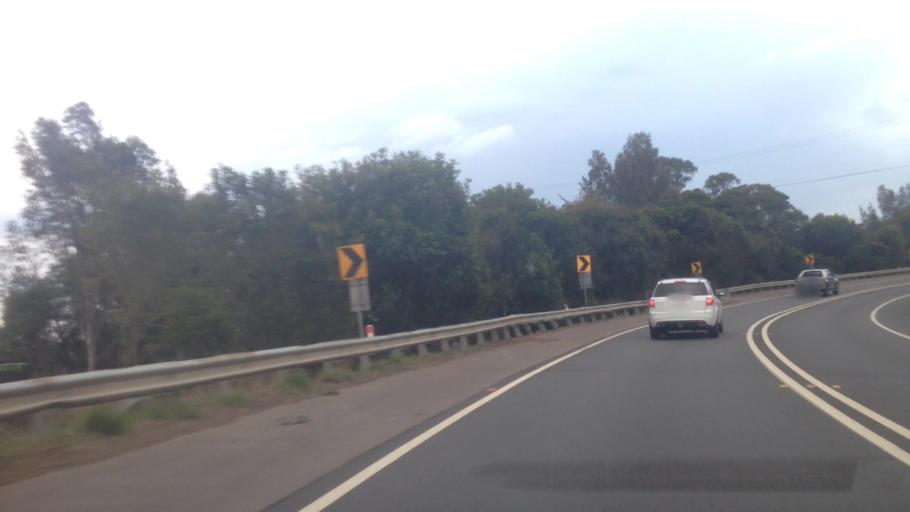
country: AU
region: New South Wales
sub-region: Wyong Shire
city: Tuggerawong
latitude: -33.2626
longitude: 151.4557
